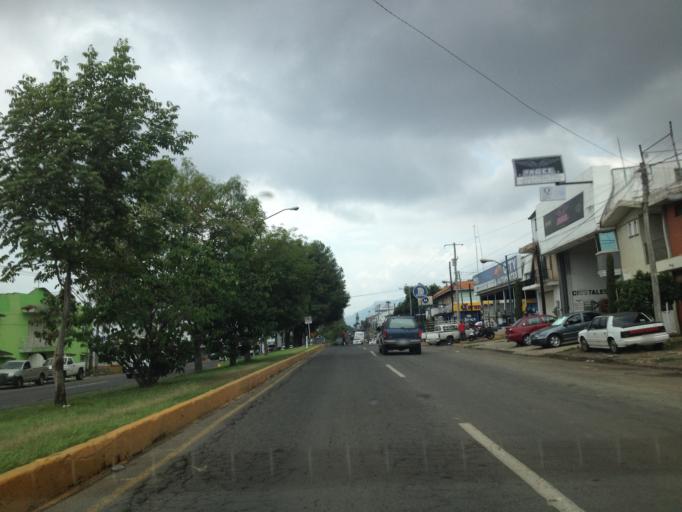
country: MX
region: Michoacan
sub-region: Uruapan
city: Uruapan
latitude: 19.4293
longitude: -102.0320
